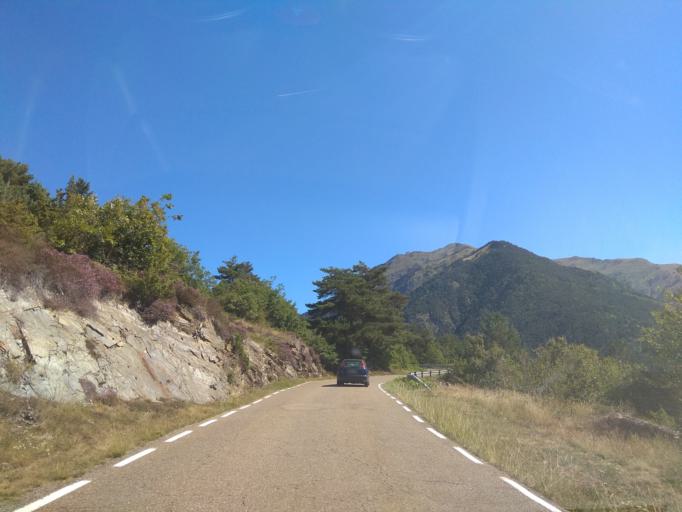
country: ES
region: Catalonia
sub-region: Provincia de Lleida
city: Vielha
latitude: 42.7410
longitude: 0.7458
